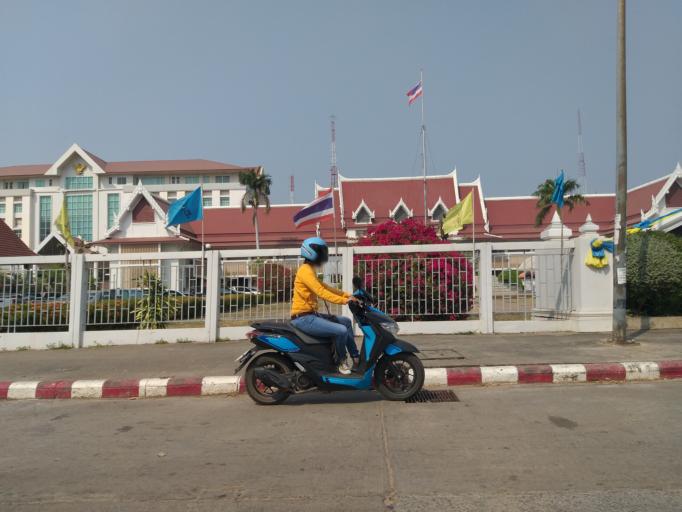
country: TH
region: Khon Kaen
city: Khon Kaen
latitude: 16.4408
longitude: 102.8320
